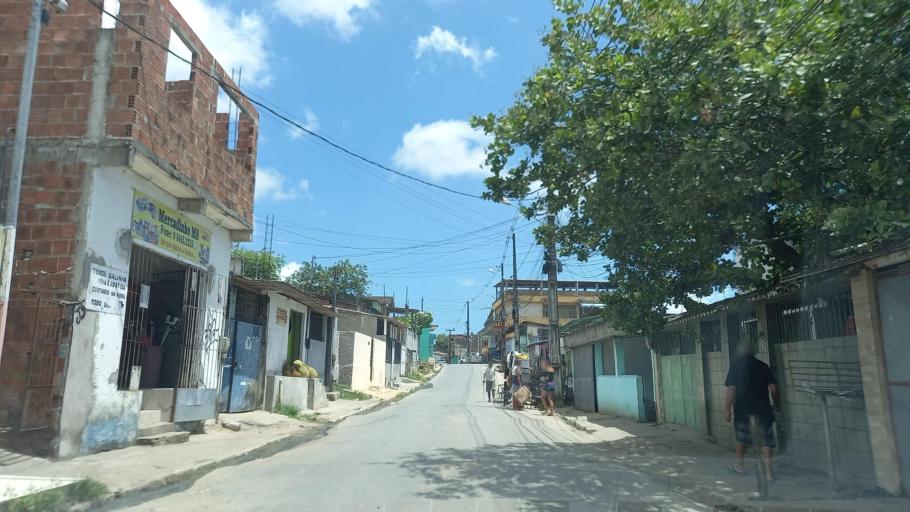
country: BR
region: Pernambuco
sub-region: Jaboatao Dos Guararapes
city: Jaboatao
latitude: -8.1741
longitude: -35.0023
